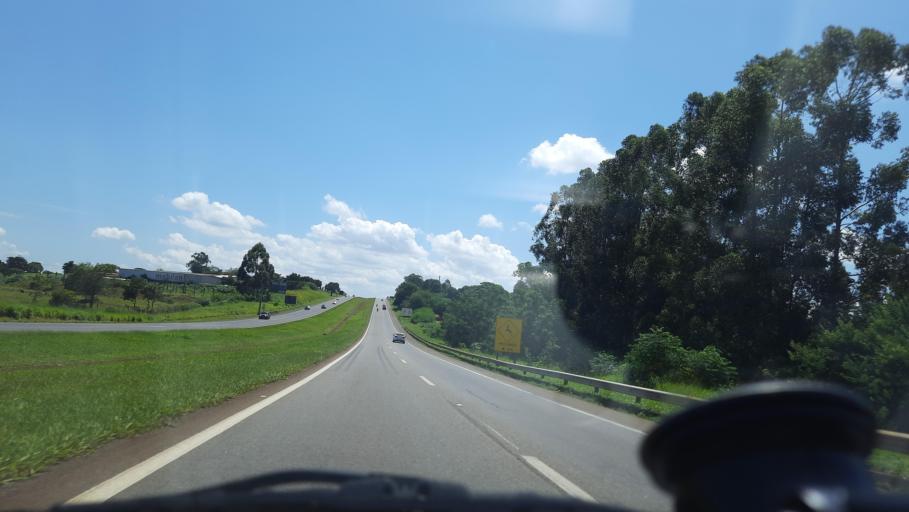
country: BR
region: Sao Paulo
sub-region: Mogi-Mirim
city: Mogi Mirim
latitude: -22.4326
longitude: -46.9845
